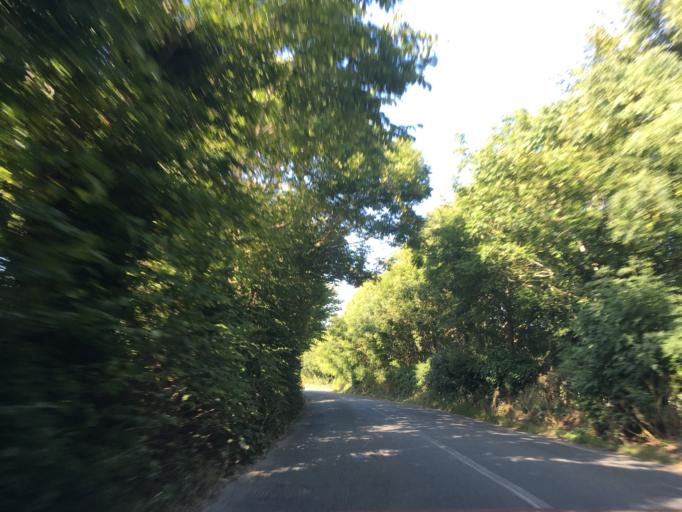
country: IE
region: Leinster
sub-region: Loch Garman
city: Loch Garman
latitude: 52.2668
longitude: -6.4782
